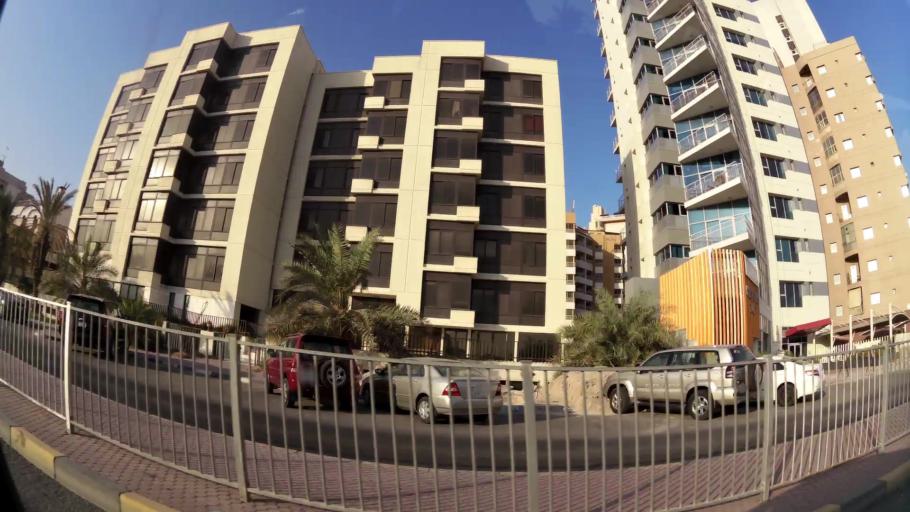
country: KW
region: Muhafazat Hawalli
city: As Salimiyah
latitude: 29.3239
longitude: 48.0877
